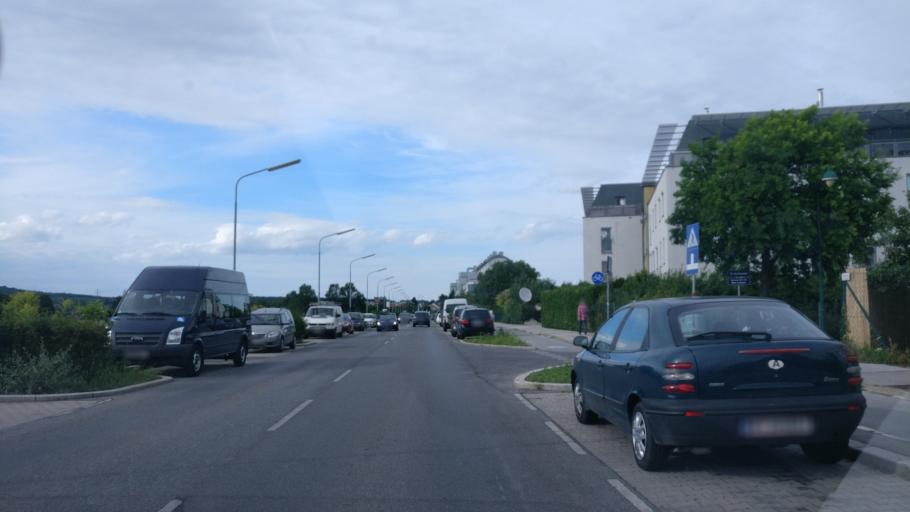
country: AT
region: Lower Austria
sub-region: Politischer Bezirk Korneuburg
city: Hagenbrunn
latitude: 48.2861
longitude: 16.4099
